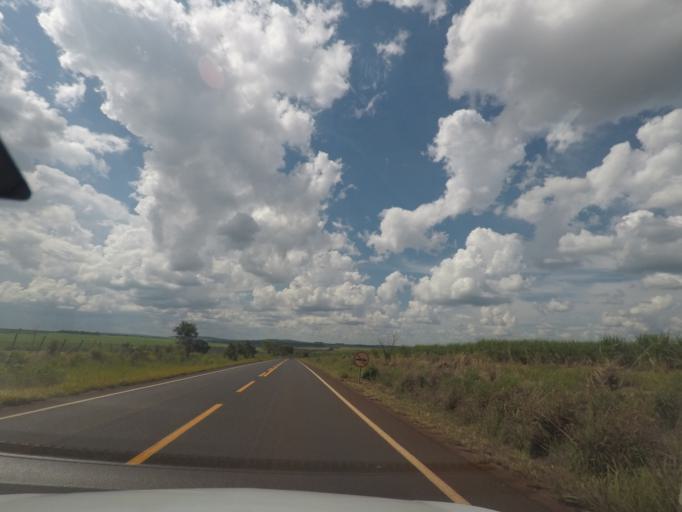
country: BR
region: Minas Gerais
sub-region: Conceicao Das Alagoas
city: Conceicao das Alagoas
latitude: -19.8250
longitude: -48.5919
